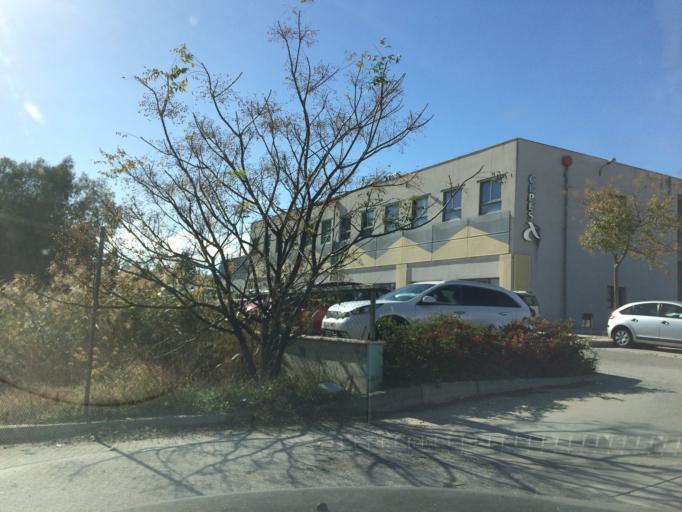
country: ES
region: Andalusia
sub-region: Provincia de Malaga
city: Alhaurin de la Torre
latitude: 36.7319
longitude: -4.5471
